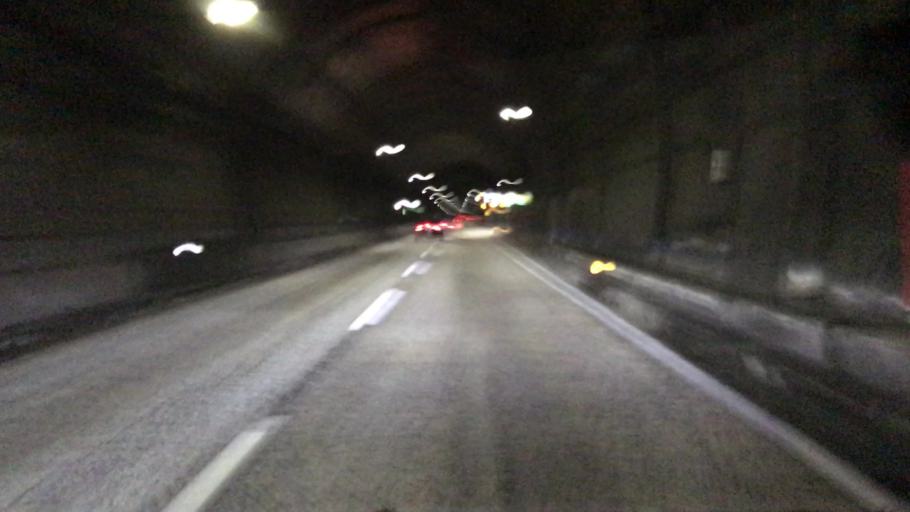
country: JP
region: Hyogo
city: Kobe
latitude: 34.7357
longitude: 135.1759
